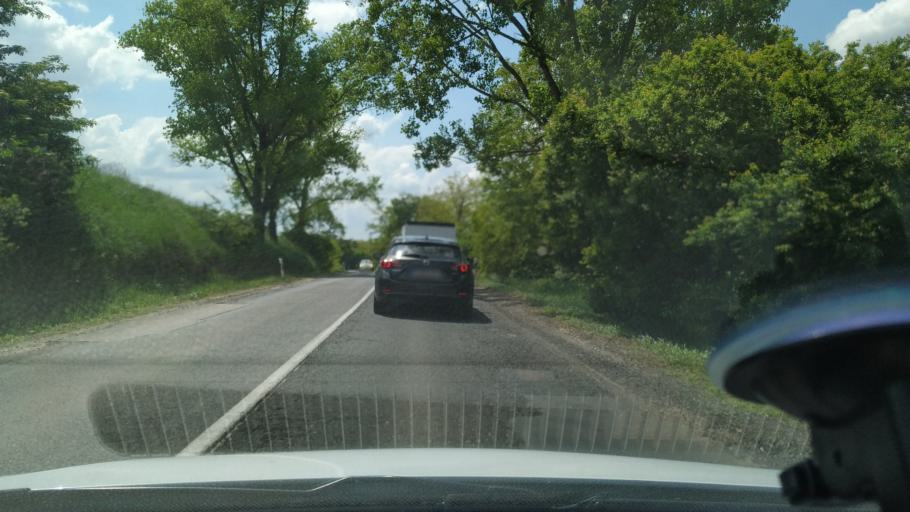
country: HU
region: Pest
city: Mende
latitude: 47.4390
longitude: 19.4777
